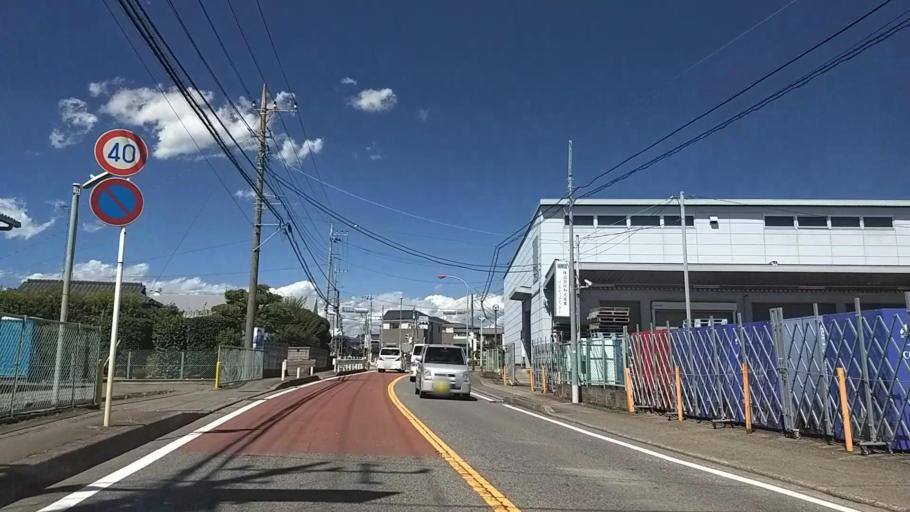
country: JP
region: Tokyo
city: Hachioji
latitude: 35.5754
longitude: 139.3161
